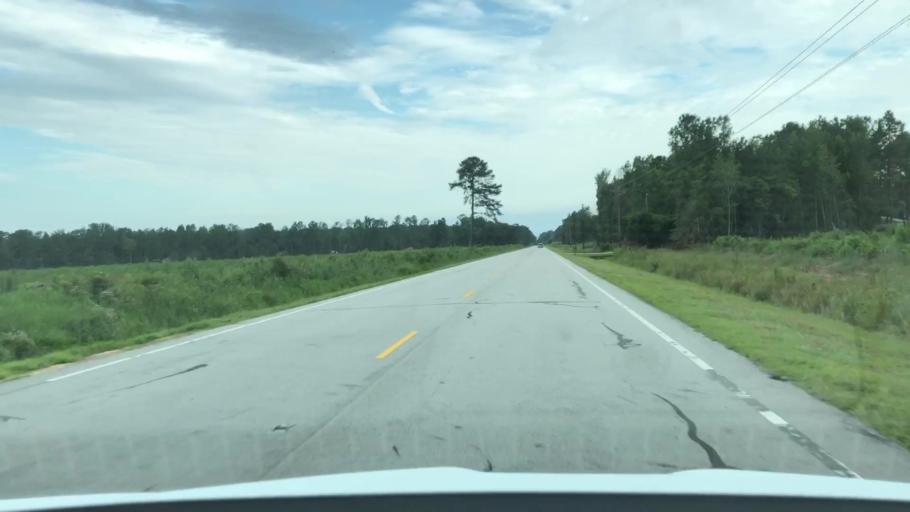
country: US
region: North Carolina
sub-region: Lenoir County
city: Kinston
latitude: 35.1269
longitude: -77.5214
